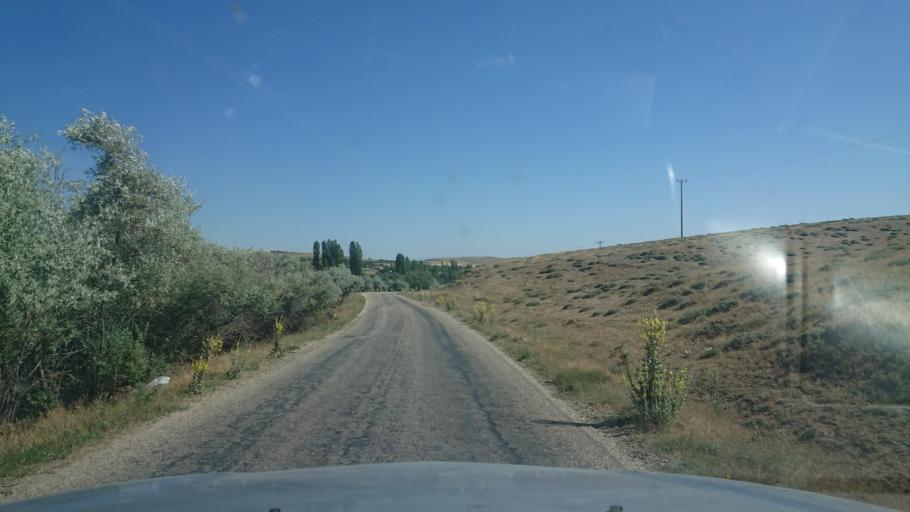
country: TR
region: Aksaray
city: Agacoren
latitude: 38.8771
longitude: 33.8808
